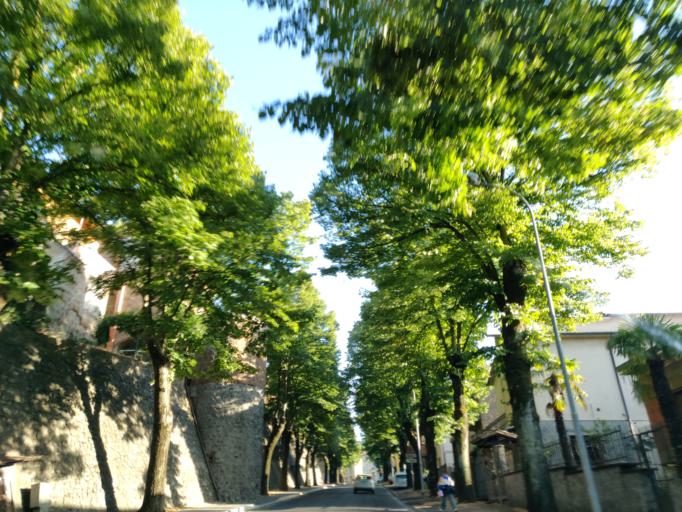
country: IT
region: Latium
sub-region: Provincia di Viterbo
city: Acquapendente
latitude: 42.7455
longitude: 11.8630
